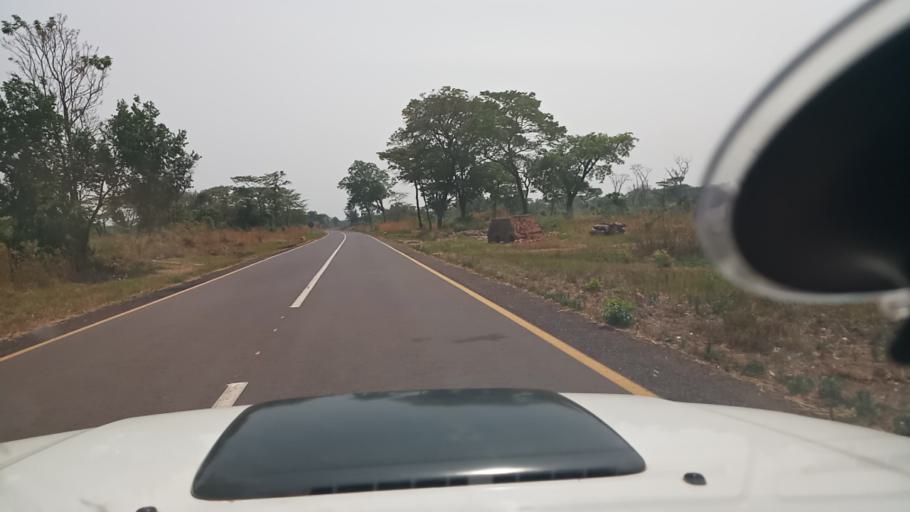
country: ZM
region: Luapula
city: Mwense
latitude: -10.7870
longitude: 28.2382
